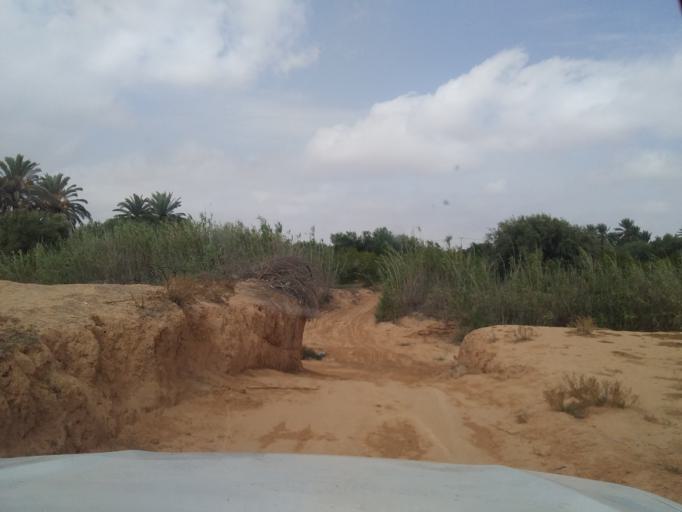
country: TN
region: Qabis
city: Gabes
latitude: 33.6270
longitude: 10.2952
